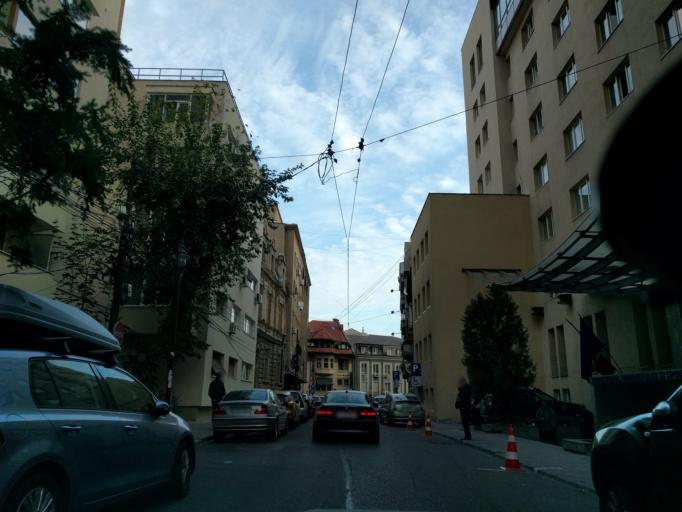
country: RO
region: Bucuresti
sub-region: Municipiul Bucuresti
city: Bucharest
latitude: 44.4402
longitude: 26.1013
